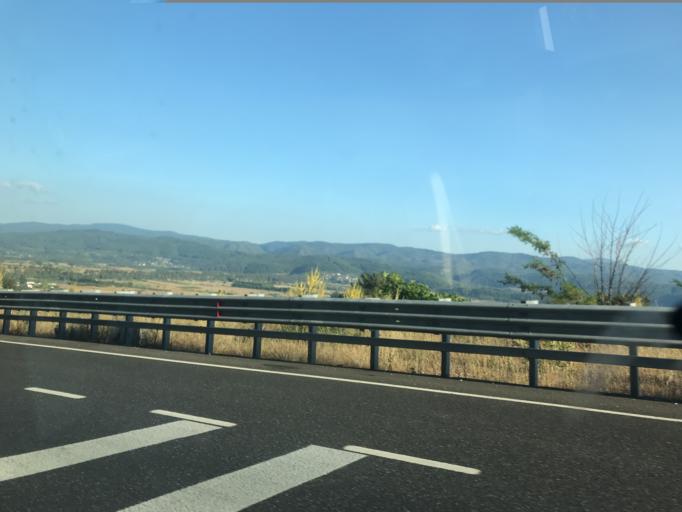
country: TR
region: Mugla
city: Yerkesik
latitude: 37.0593
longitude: 28.3413
